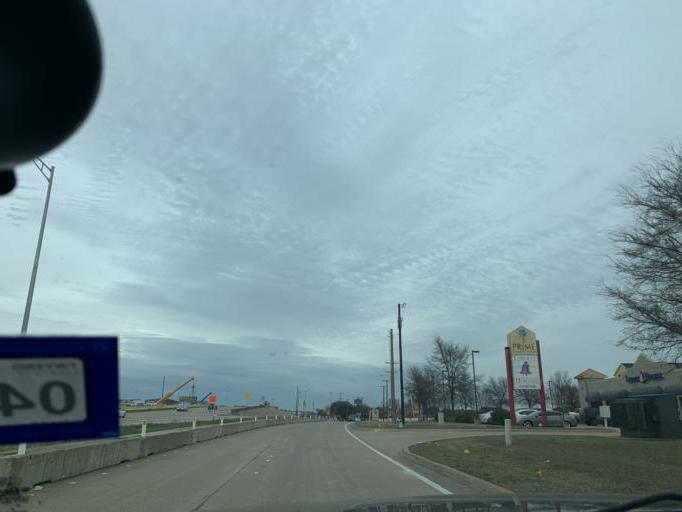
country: US
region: Texas
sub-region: Dallas County
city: Duncanville
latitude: 32.6452
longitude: -96.8866
